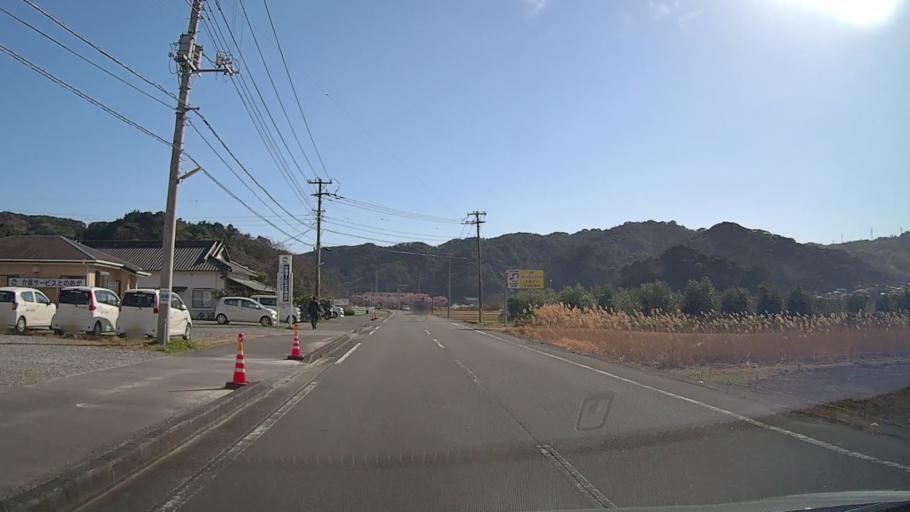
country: JP
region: Shizuoka
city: Shimoda
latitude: 34.6711
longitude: 138.9133
